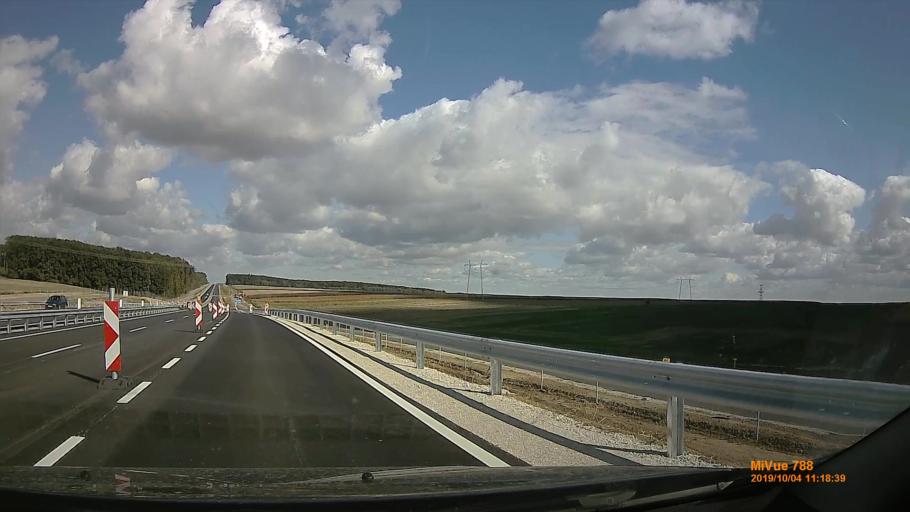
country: HU
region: Somogy
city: Kaposvar
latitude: 46.4734
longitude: 17.8029
